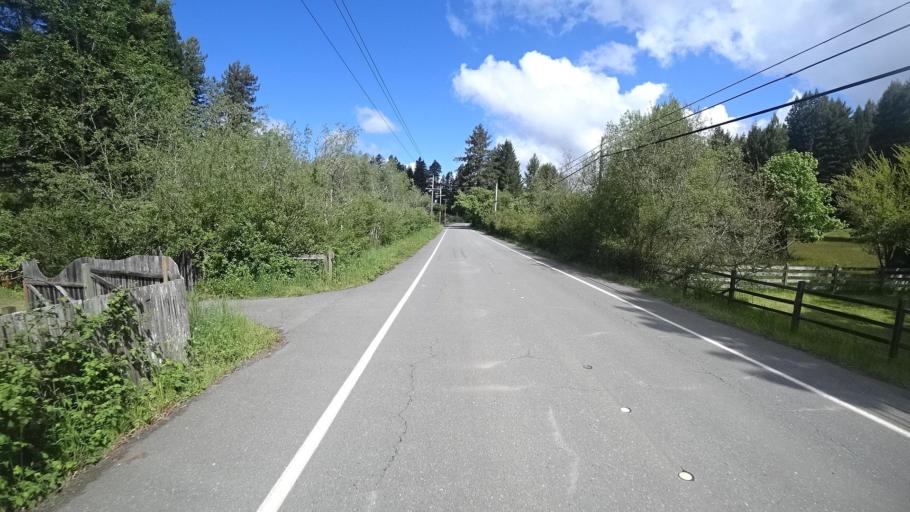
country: US
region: California
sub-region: Humboldt County
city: McKinleyville
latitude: 40.9519
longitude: -124.0329
